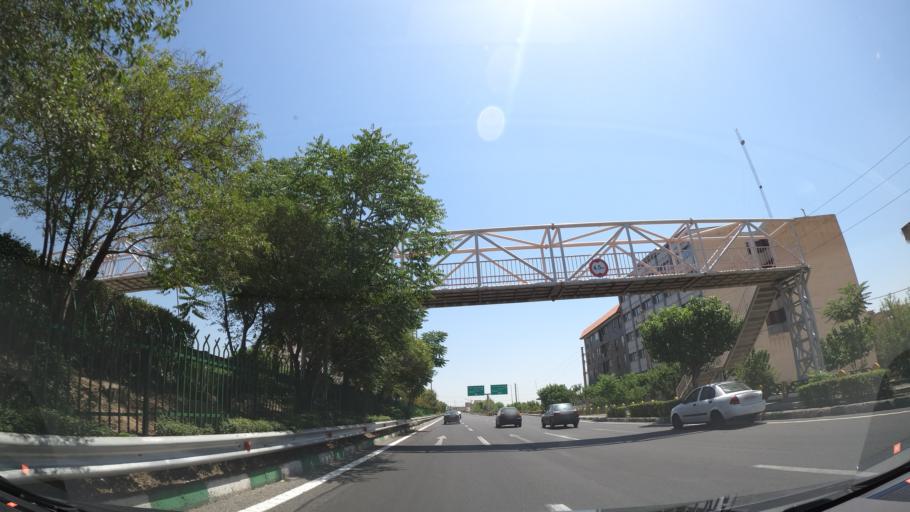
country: IR
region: Tehran
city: Tajrish
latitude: 35.7630
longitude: 51.2932
